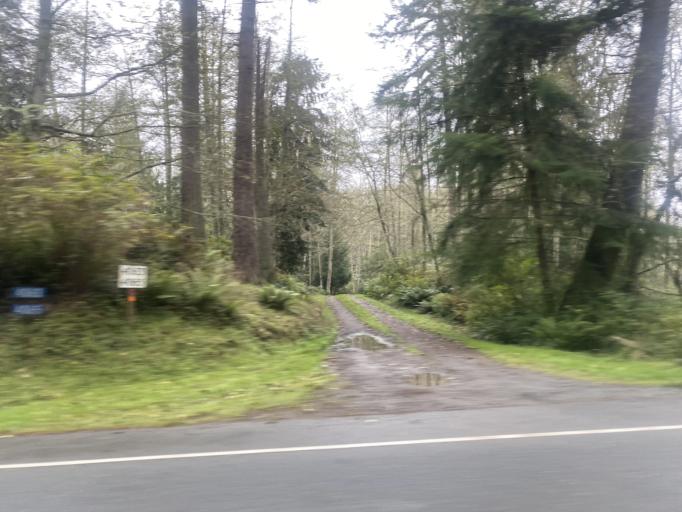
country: US
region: Washington
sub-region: Island County
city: Freeland
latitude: 48.0638
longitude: -122.5068
